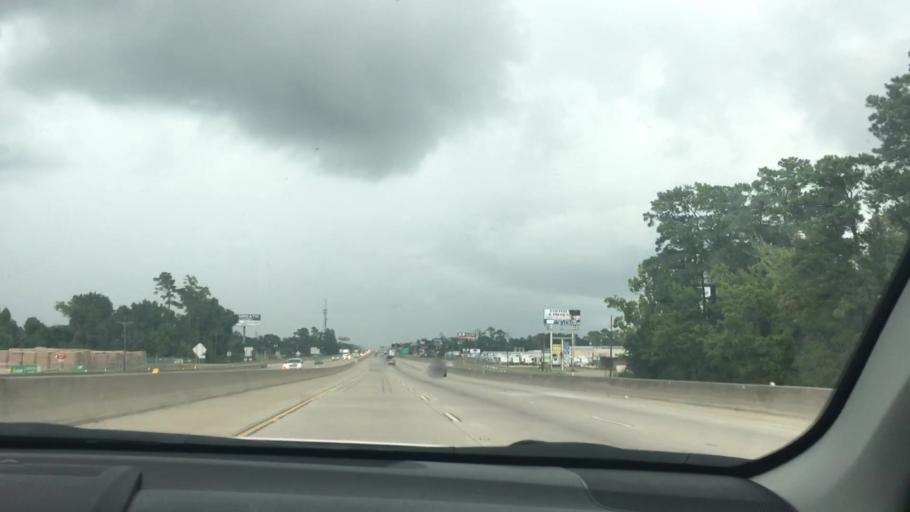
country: US
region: Texas
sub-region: Jefferson County
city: Beaumont
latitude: 30.1030
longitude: -94.0588
